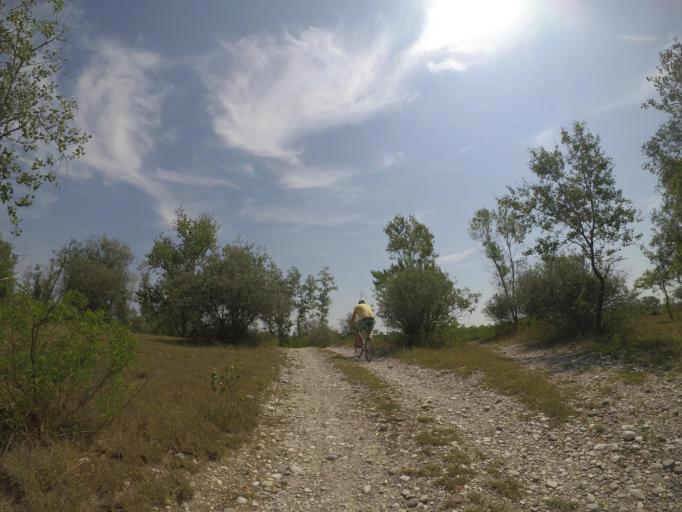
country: IT
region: Friuli Venezia Giulia
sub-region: Provincia di Pordenone
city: Rosa
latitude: 45.9408
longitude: 12.9021
